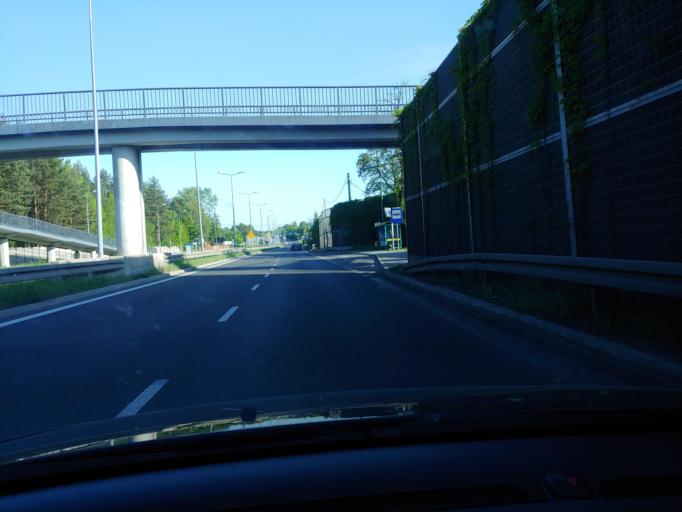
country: PL
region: Silesian Voivodeship
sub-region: Jaworzno
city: Jaworzno
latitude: 50.1836
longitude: 19.2893
